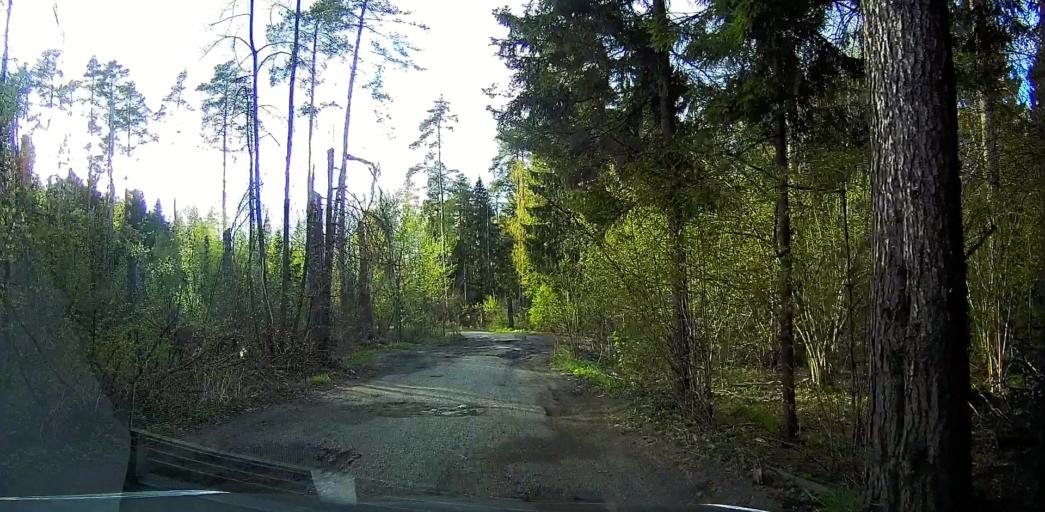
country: RU
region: Moskovskaya
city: Malyshevo
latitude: 55.5549
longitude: 38.3381
